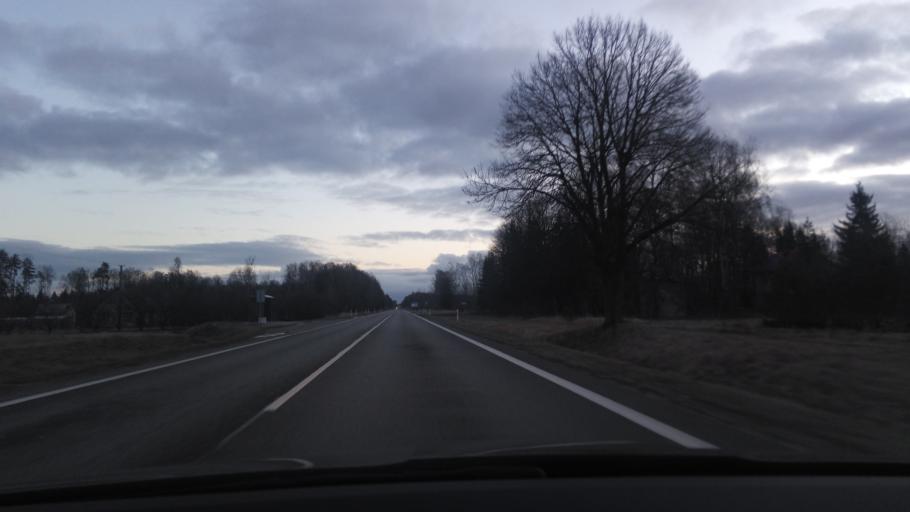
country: LT
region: Kauno apskritis
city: Jonava
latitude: 55.1511
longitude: 24.4732
